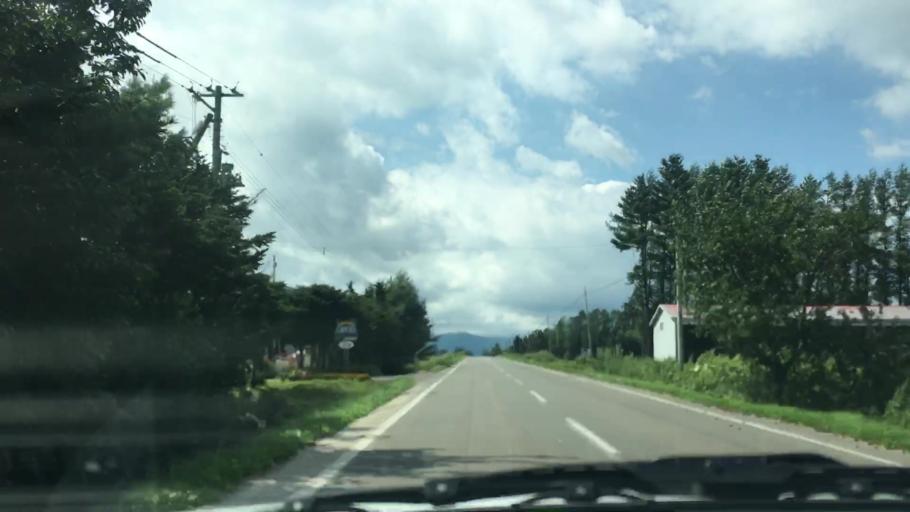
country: JP
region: Hokkaido
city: Otofuke
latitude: 43.2772
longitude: 143.3648
